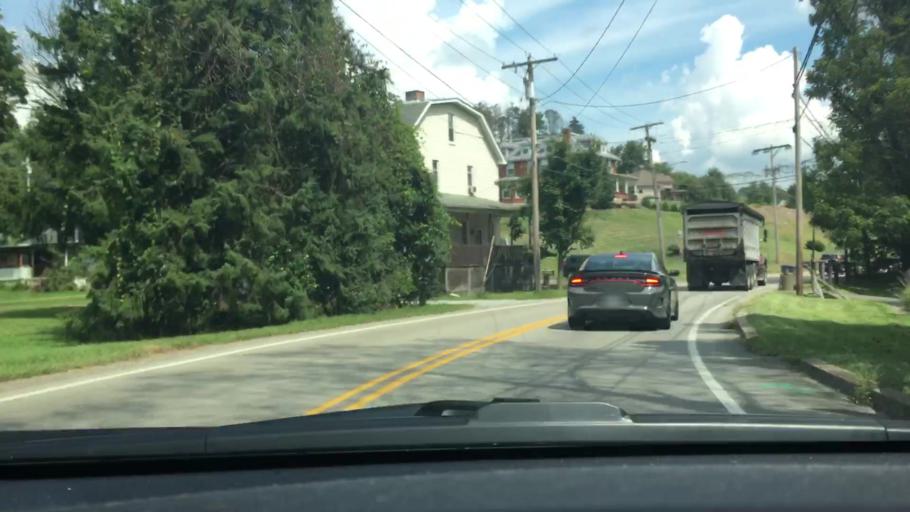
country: US
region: Pennsylvania
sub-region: Washington County
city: Gastonville
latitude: 40.2467
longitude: -80.0436
